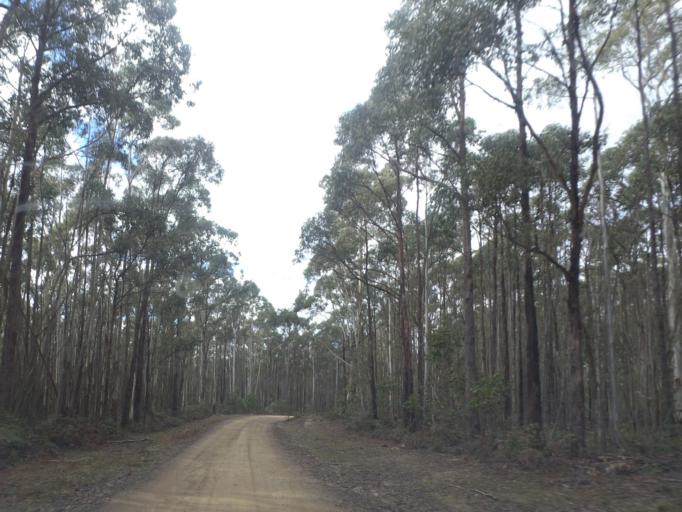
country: AU
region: Victoria
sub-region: Moorabool
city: Bacchus Marsh
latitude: -37.4278
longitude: 144.4314
